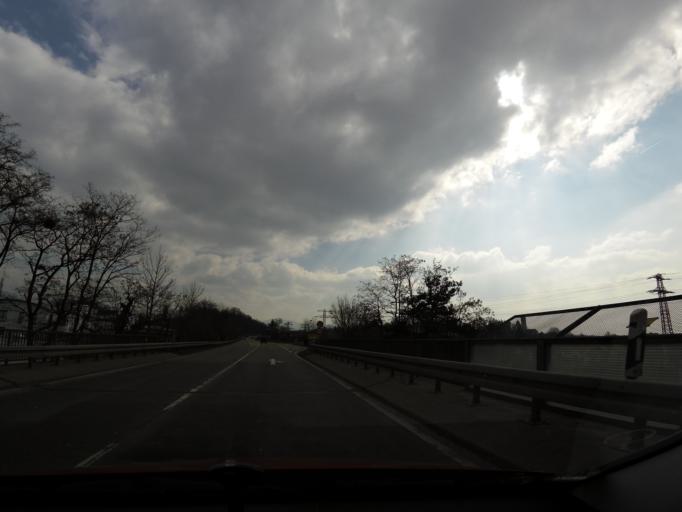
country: DE
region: Baden-Wuerttemberg
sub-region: Freiburg Region
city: Achern
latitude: 48.6284
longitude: 8.0532
